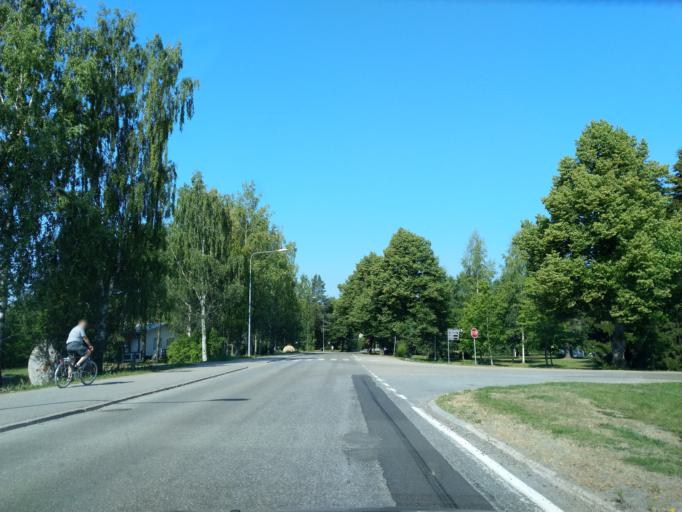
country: FI
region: Satakunta
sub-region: Pori
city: Noormarkku
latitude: 61.5909
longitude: 21.8819
